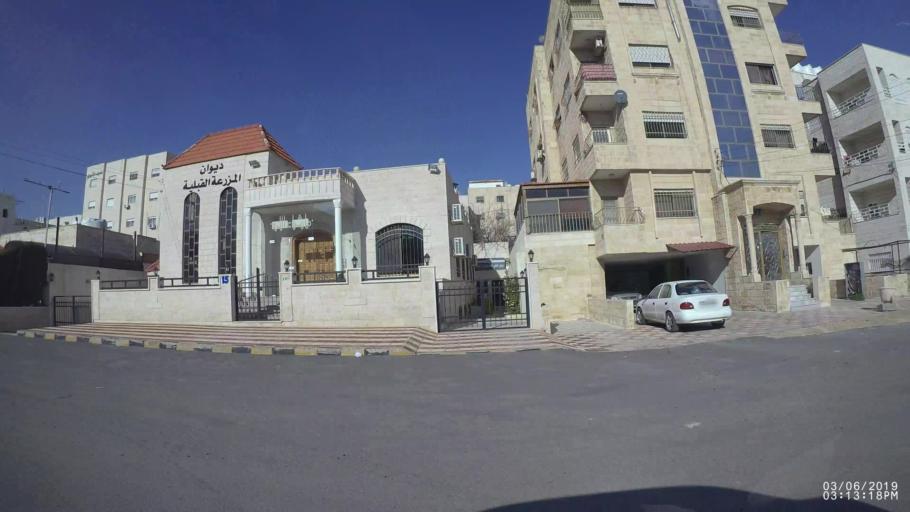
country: JO
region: Amman
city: Amman
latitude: 31.9784
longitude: 35.9349
